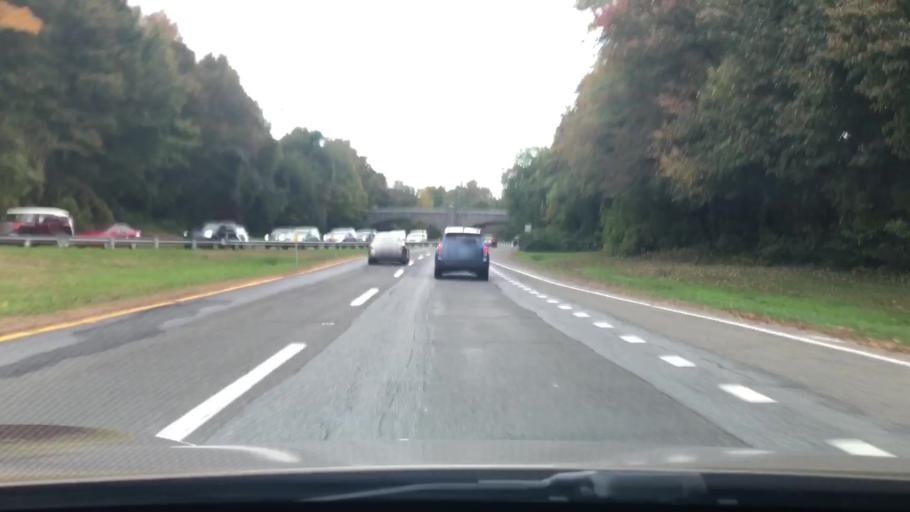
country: US
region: New York
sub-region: Westchester County
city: Tuckahoe
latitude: 40.9553
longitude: -73.8315
